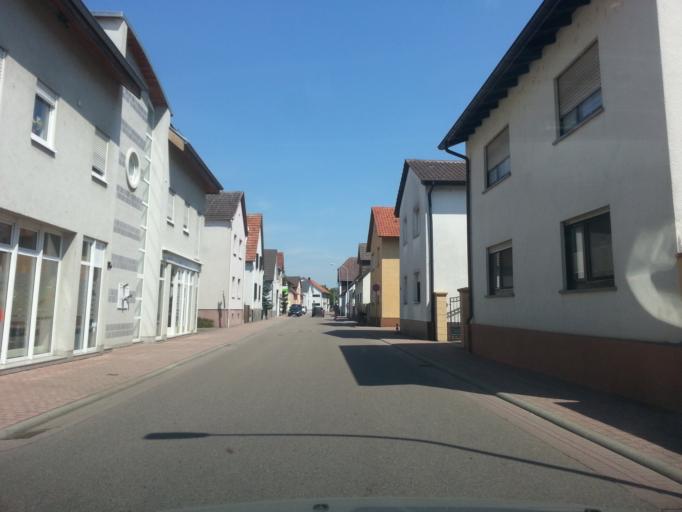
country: DE
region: Hesse
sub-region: Regierungsbezirk Darmstadt
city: Einhausen
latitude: 49.6701
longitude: 8.5433
